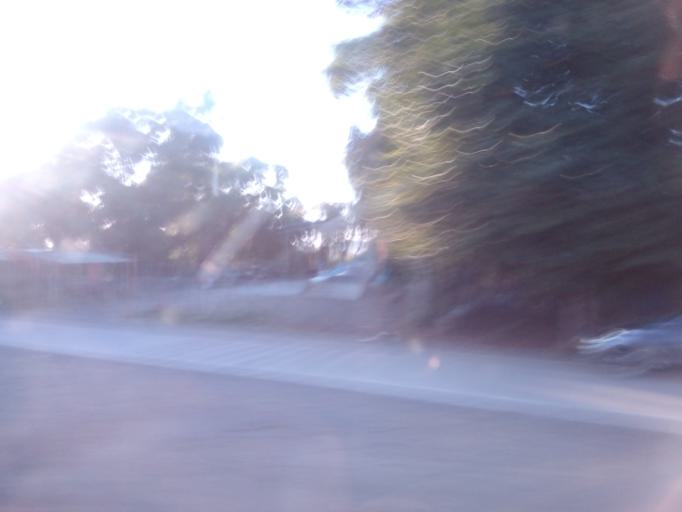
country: PA
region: Veraguas
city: Atalaya
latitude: 8.0805
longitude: -80.8975
